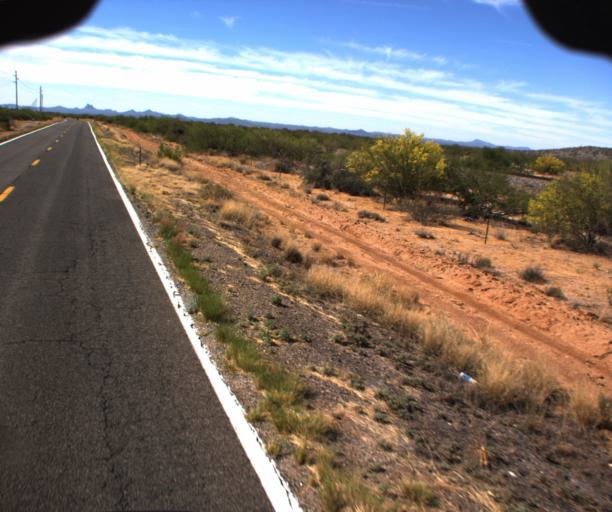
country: US
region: Arizona
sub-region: Yavapai County
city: Congress
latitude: 34.1384
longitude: -112.8410
